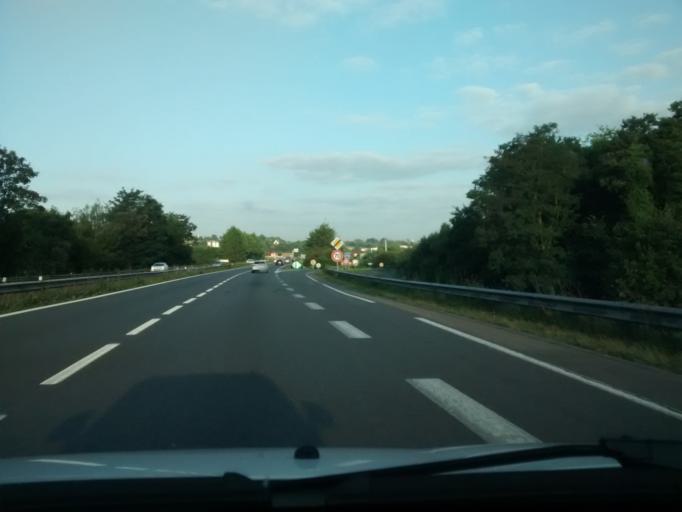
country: FR
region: Brittany
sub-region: Departement des Cotes-d'Armor
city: Yffiniac
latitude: 48.4793
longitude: -2.6676
